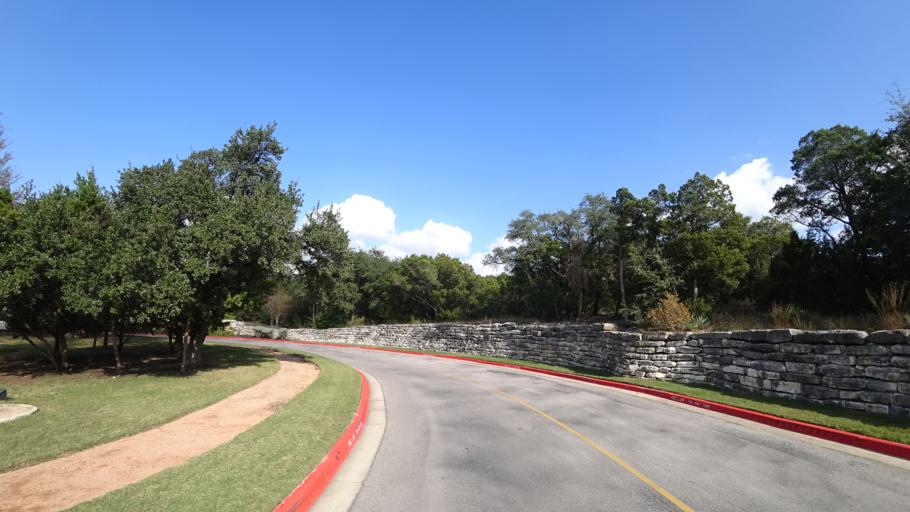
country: US
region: Texas
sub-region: Travis County
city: Barton Creek
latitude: 30.2898
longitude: -97.8677
